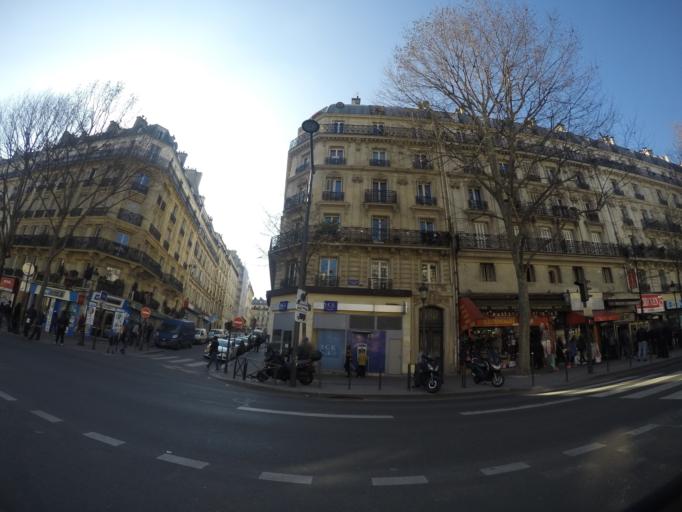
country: FR
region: Ile-de-France
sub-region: Paris
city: Saint-Ouen
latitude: 48.8865
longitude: 2.3497
